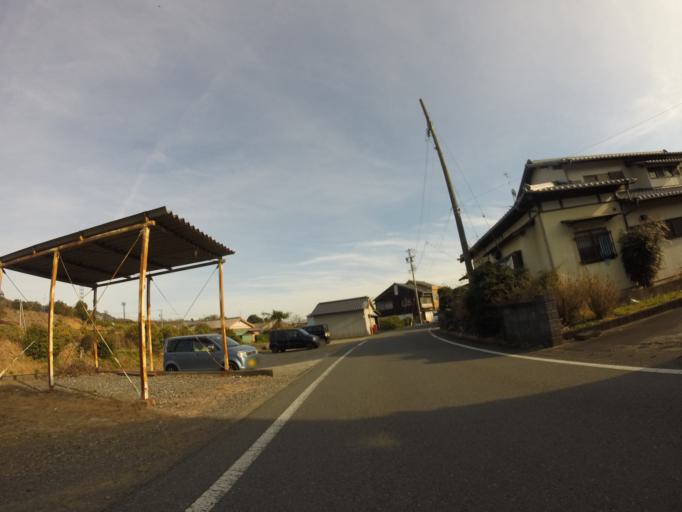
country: JP
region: Shizuoka
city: Shizuoka-shi
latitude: 35.0542
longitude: 138.4756
